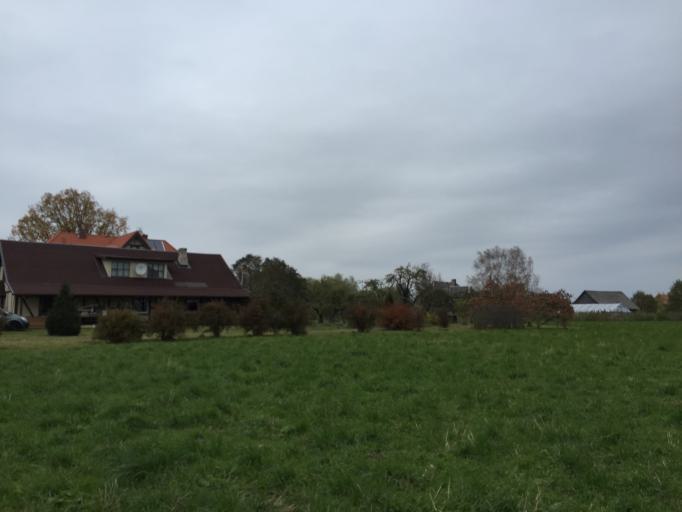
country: LV
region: Ozolnieku
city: Ozolnieki
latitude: 56.6383
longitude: 23.7783
